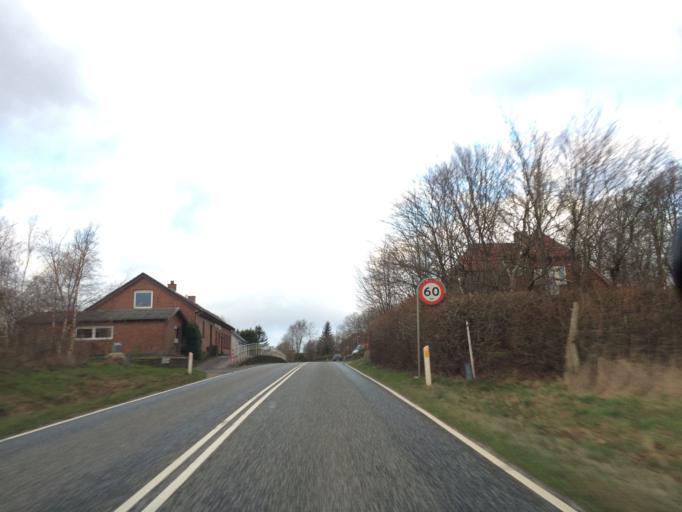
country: DK
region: Central Jutland
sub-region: Silkeborg Kommune
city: Svejbaek
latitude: 56.0986
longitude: 9.6084
